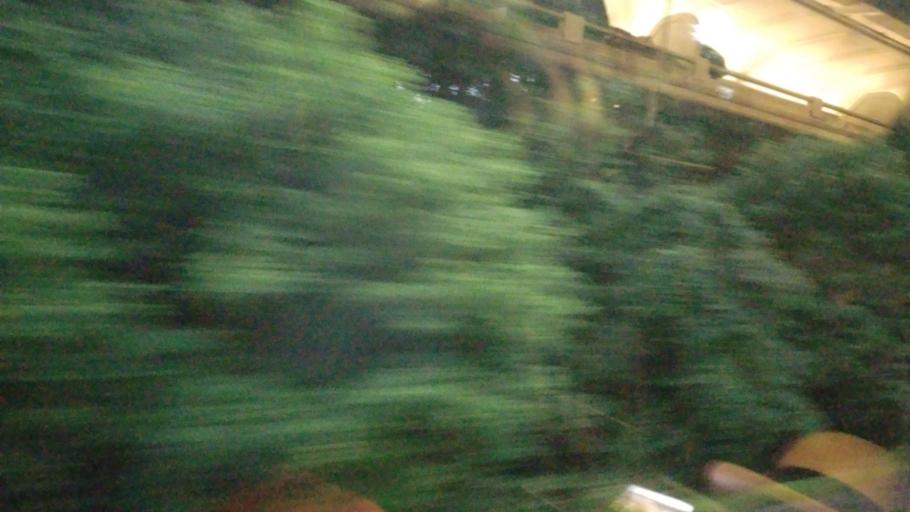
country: US
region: Virginia
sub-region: Orange County
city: Orange
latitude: 38.2415
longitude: -78.1280
